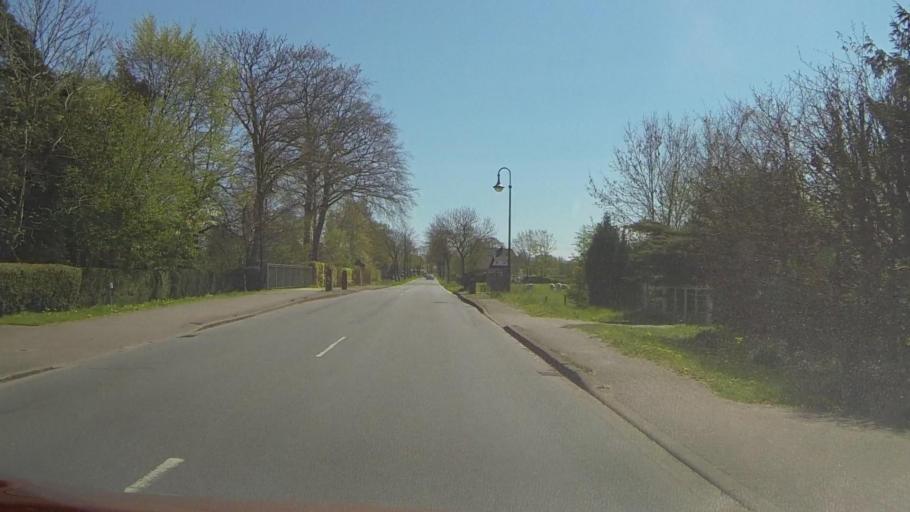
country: DE
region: Schleswig-Holstein
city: Ellerbek
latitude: 53.6553
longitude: 9.8697
